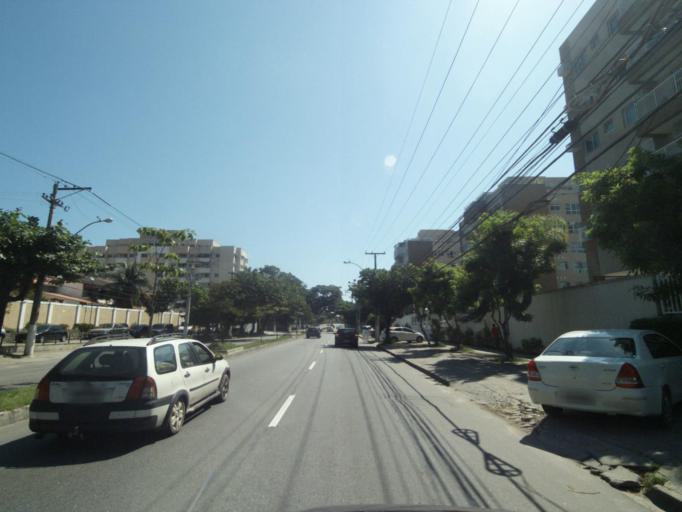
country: BR
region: Rio de Janeiro
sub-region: Niteroi
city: Niteroi
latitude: -22.9068
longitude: -43.0578
